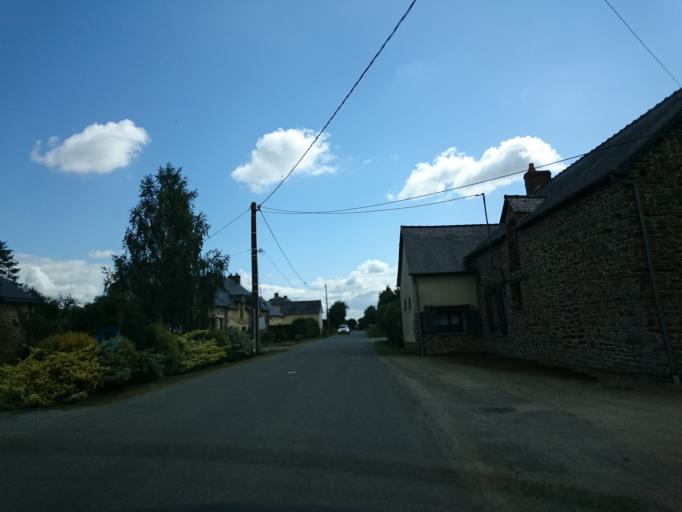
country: FR
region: Brittany
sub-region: Departement d'Ille-et-Vilaine
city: Chanteloup
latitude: 47.9601
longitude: -1.6314
